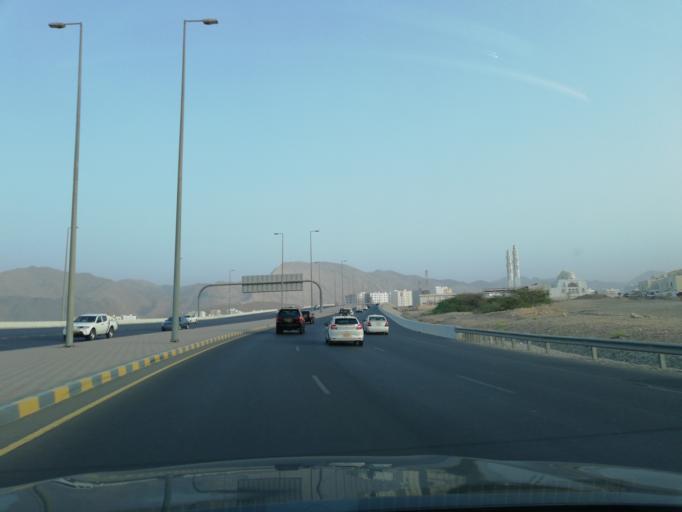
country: OM
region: Muhafazat Masqat
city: Bawshar
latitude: 23.5860
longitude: 58.4158
